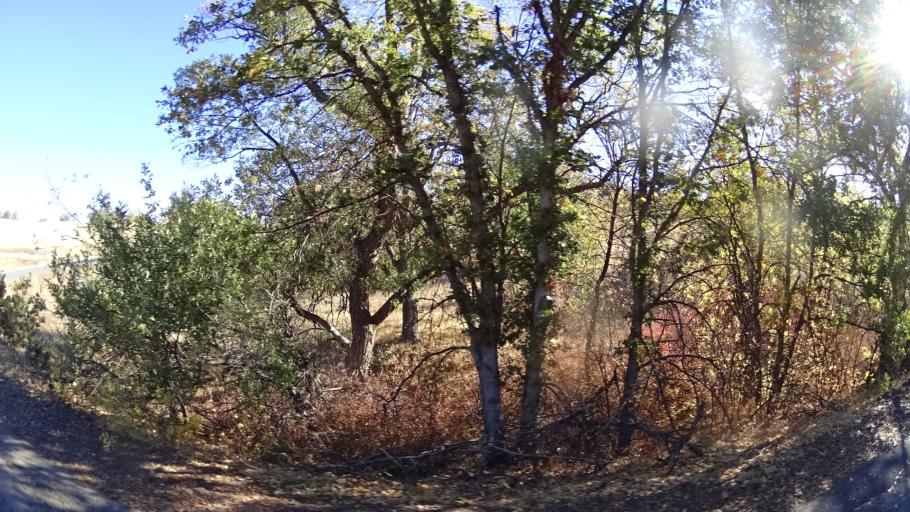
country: US
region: California
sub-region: Siskiyou County
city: Montague
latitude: 41.9497
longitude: -122.4383
